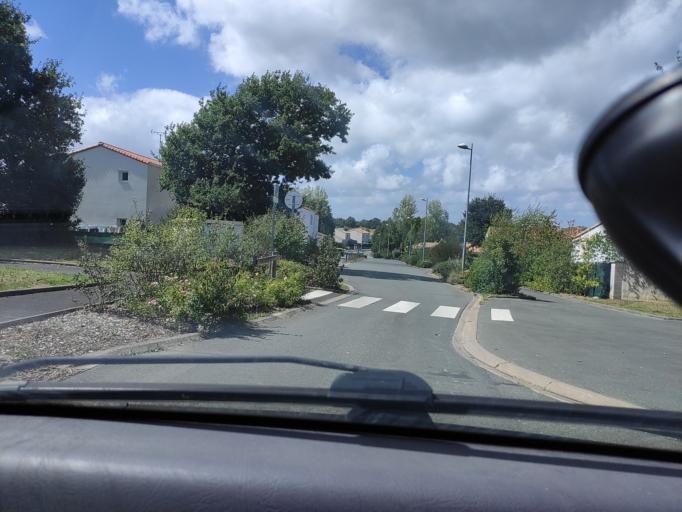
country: FR
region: Pays de la Loire
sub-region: Departement de la Vendee
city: La Roche-sur-Yon
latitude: 46.6891
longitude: -1.4472
